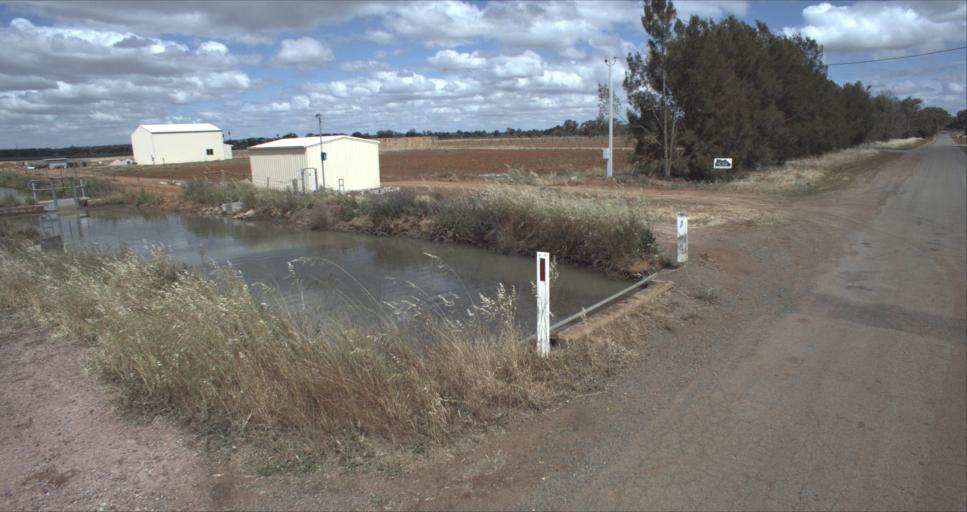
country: AU
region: New South Wales
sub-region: Leeton
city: Leeton
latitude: -34.5842
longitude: 146.3964
